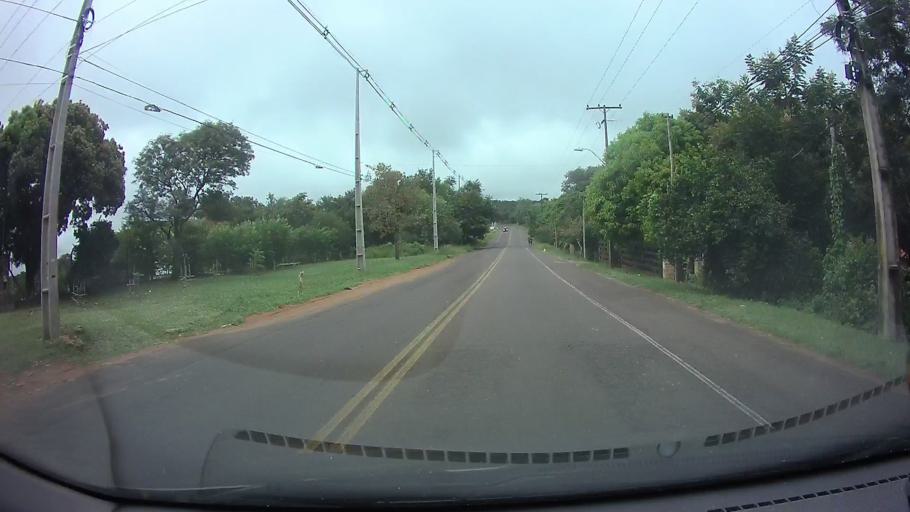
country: PY
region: Cordillera
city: Altos
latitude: -25.2885
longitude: -57.2663
